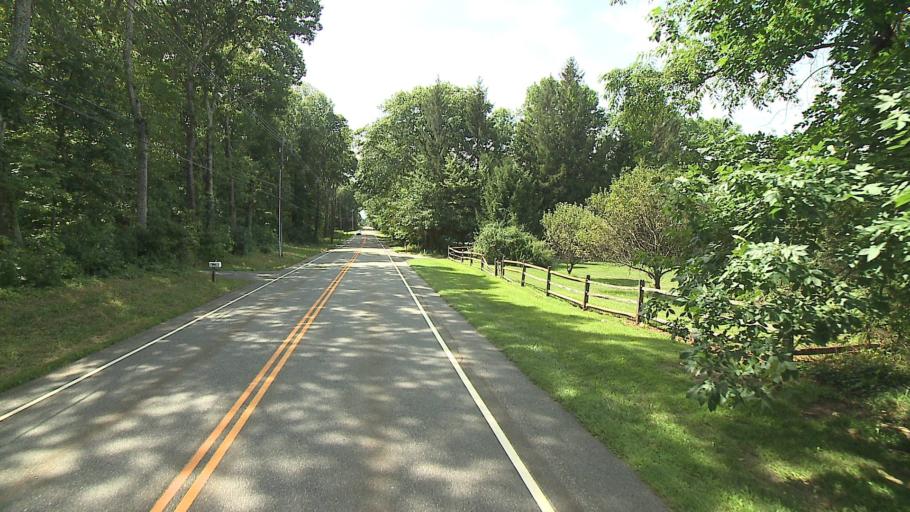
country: US
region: Connecticut
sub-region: Litchfield County
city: Bethlehem Village
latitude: 41.6581
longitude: -73.1992
